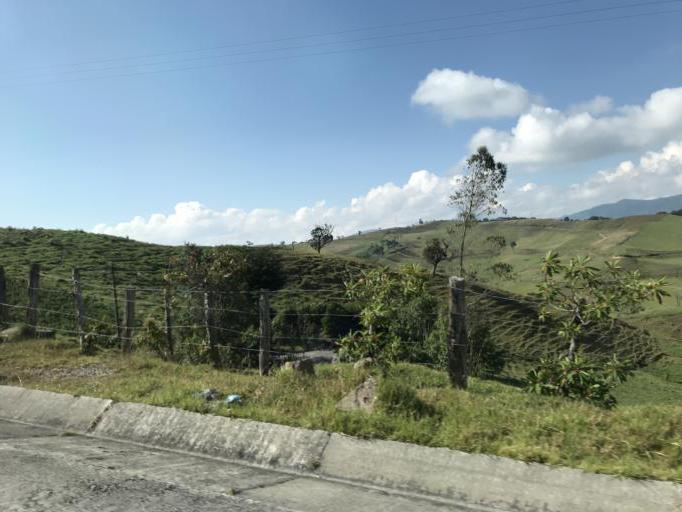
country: CO
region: Cauca
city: Paispamba
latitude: 2.2662
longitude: -76.5133
